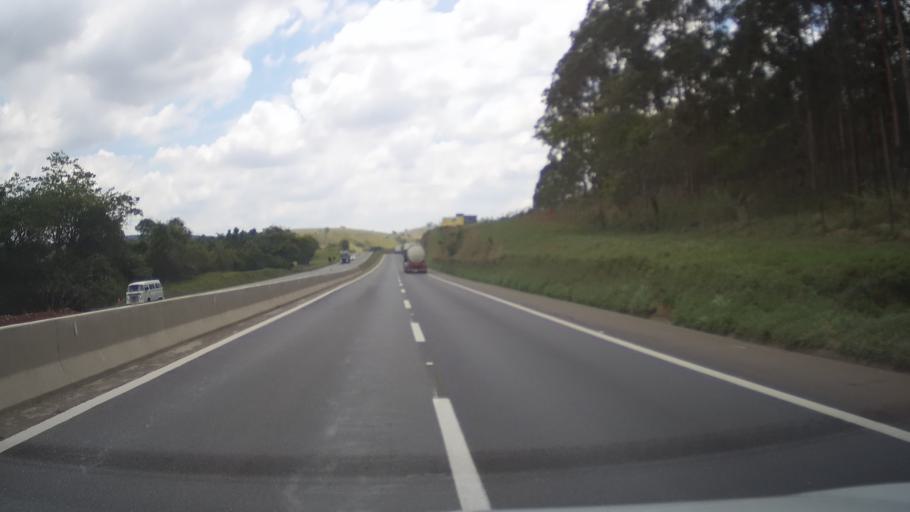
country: BR
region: Minas Gerais
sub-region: Campanha
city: Campanha
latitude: -21.7186
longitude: -45.3780
